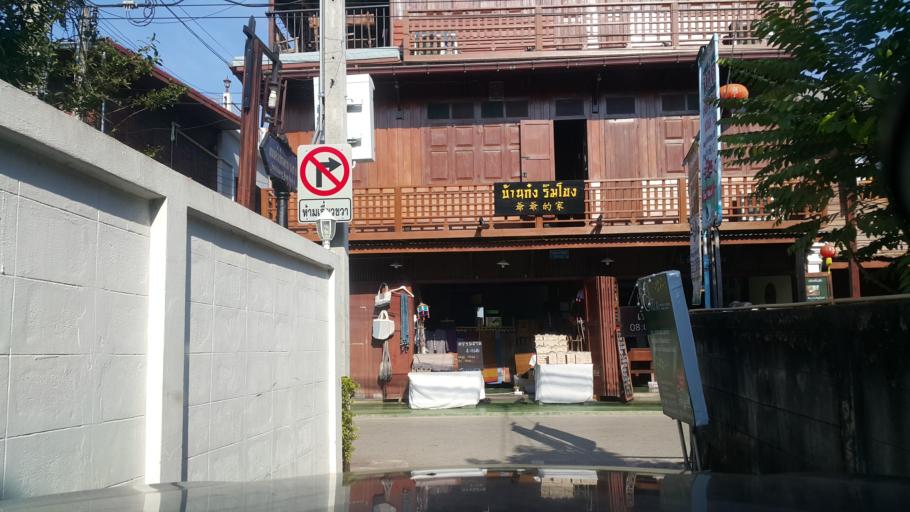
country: TH
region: Loei
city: Chiang Khan
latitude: 17.8946
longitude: 101.6536
